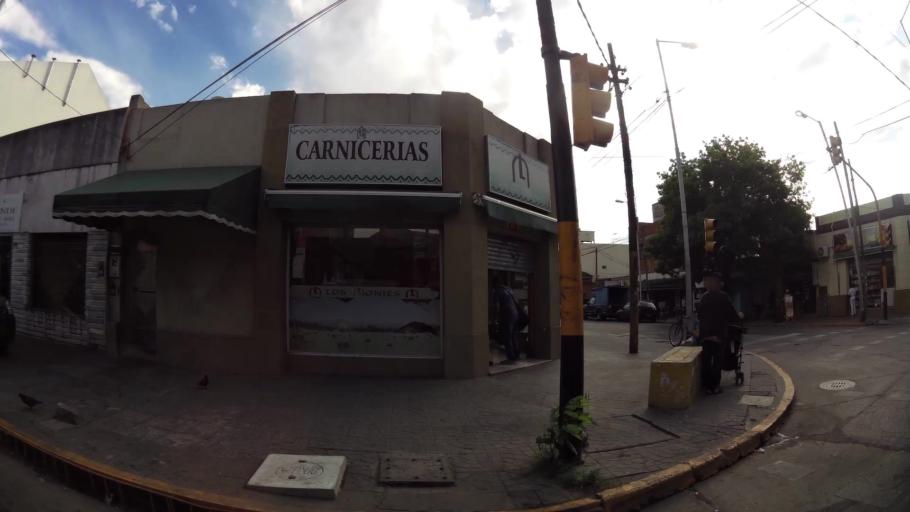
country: AR
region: Buenos Aires
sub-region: Partido de Avellaneda
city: Avellaneda
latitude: -34.6922
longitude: -58.3641
